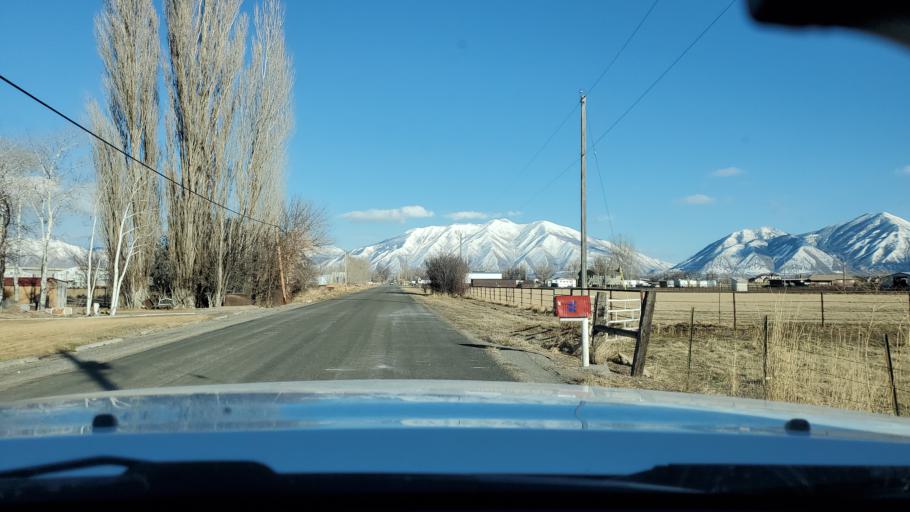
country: US
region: Utah
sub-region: Utah County
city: Benjamin
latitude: 40.1146
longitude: -111.7426
